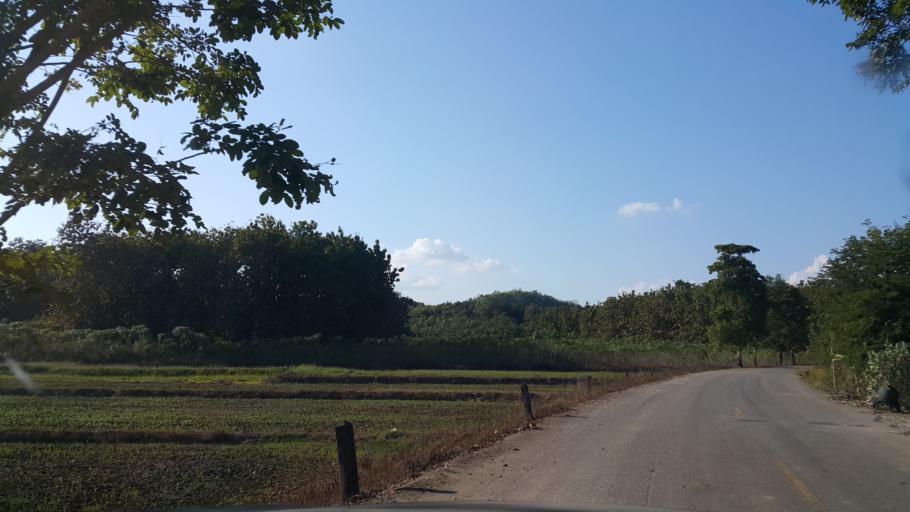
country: TH
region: Sukhothai
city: Thung Saliam
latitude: 17.3821
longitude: 99.5229
